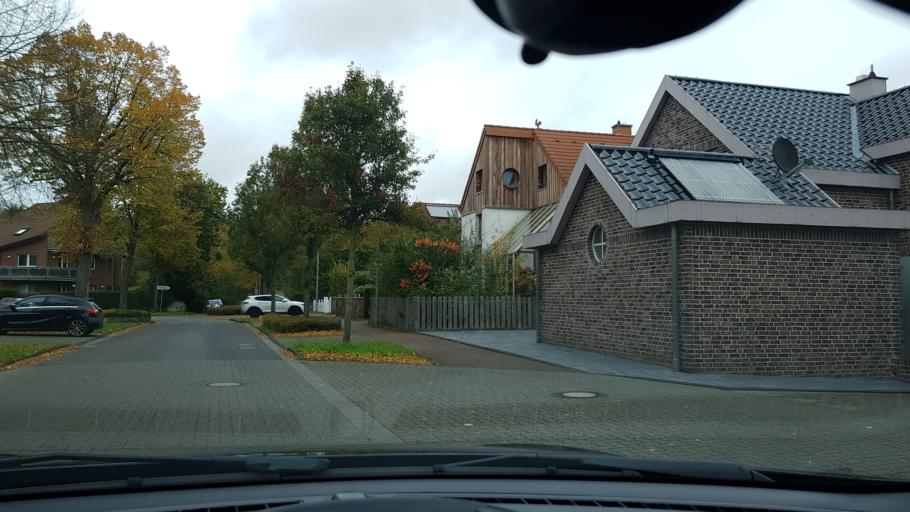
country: DE
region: North Rhine-Westphalia
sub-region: Regierungsbezirk Koln
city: Bedburg
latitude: 51.0093
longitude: 6.5470
